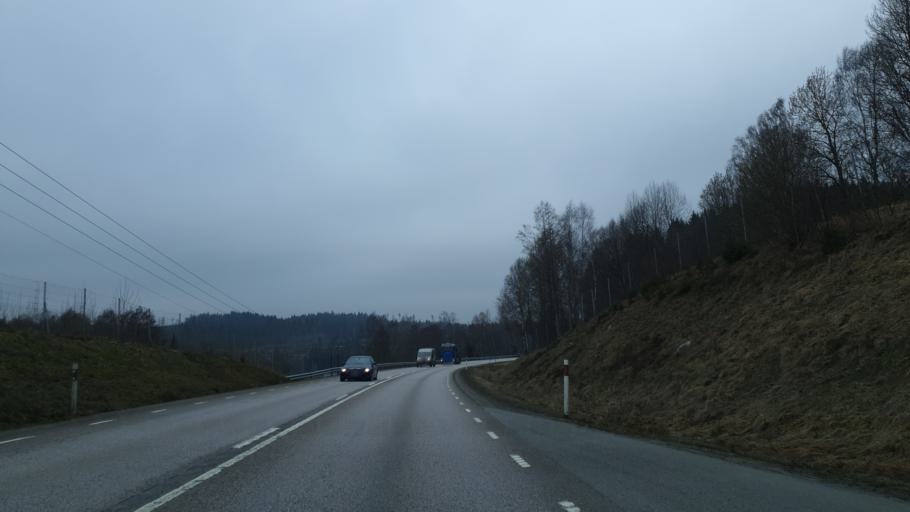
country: SE
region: Vaestra Goetaland
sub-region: Harryda Kommun
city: Hindas
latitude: 57.6258
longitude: 12.4150
